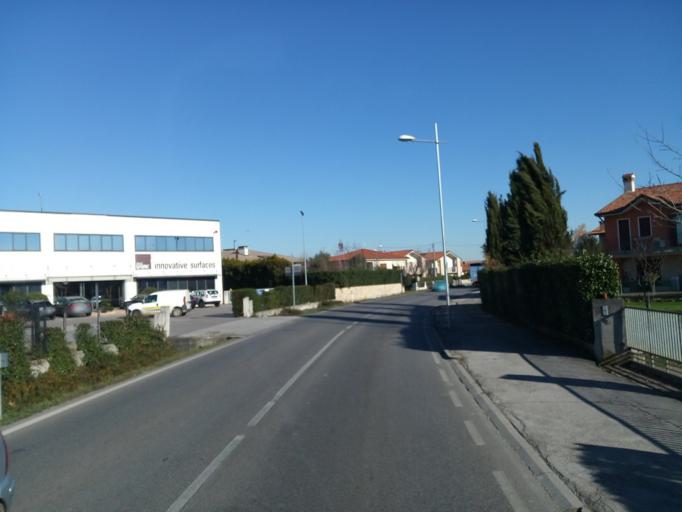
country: IT
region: Veneto
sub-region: Provincia di Treviso
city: Valla
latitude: 45.7089
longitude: 11.9296
